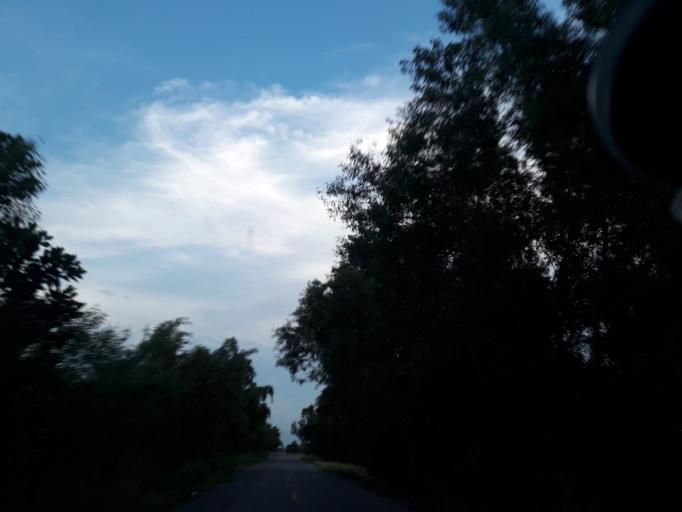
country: TH
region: Pathum Thani
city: Nong Suea
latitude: 14.2221
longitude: 100.8688
